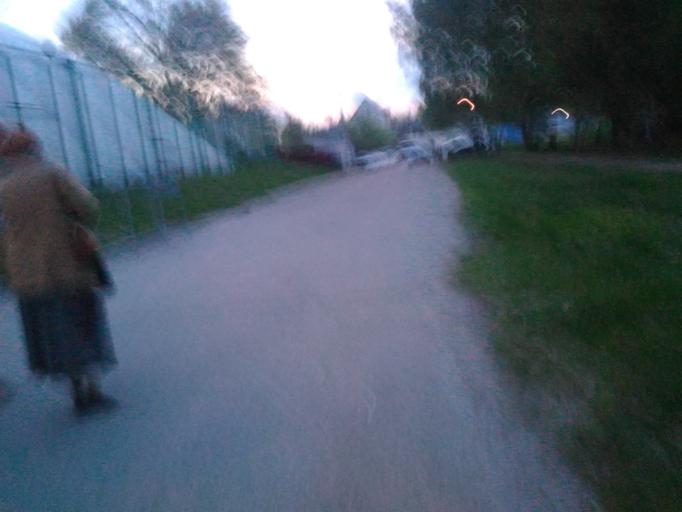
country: RU
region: Ulyanovsk
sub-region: Ulyanovskiy Rayon
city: Ulyanovsk
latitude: 54.2763
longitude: 48.3523
